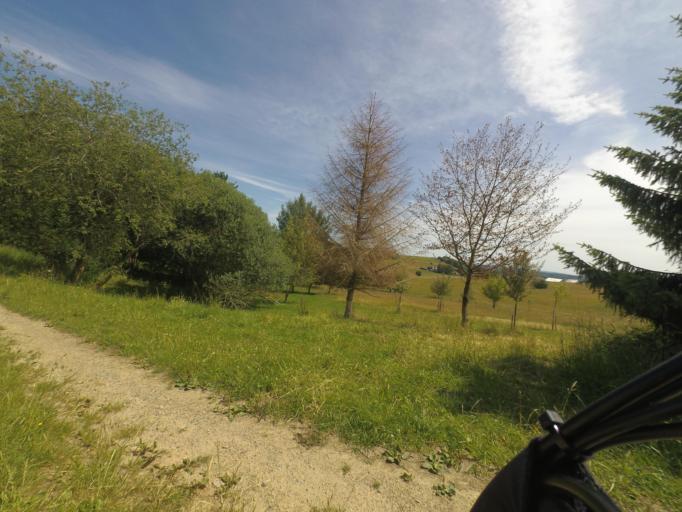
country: DE
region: Rheinland-Pfalz
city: Esch
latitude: 50.3680
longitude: 6.6066
